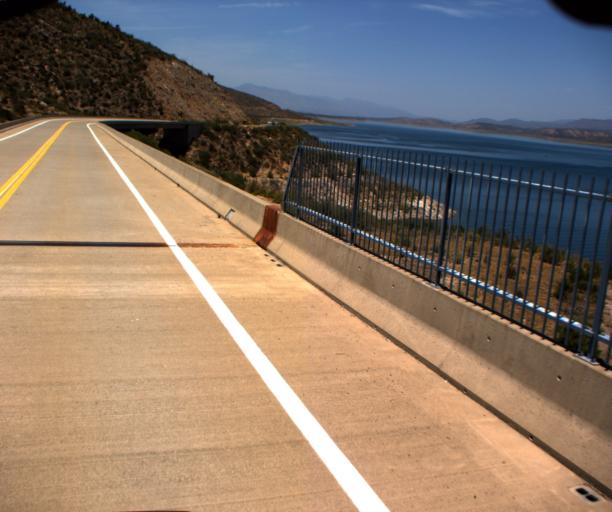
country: US
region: Arizona
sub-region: Gila County
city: Tonto Basin
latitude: 33.6748
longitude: -111.1587
